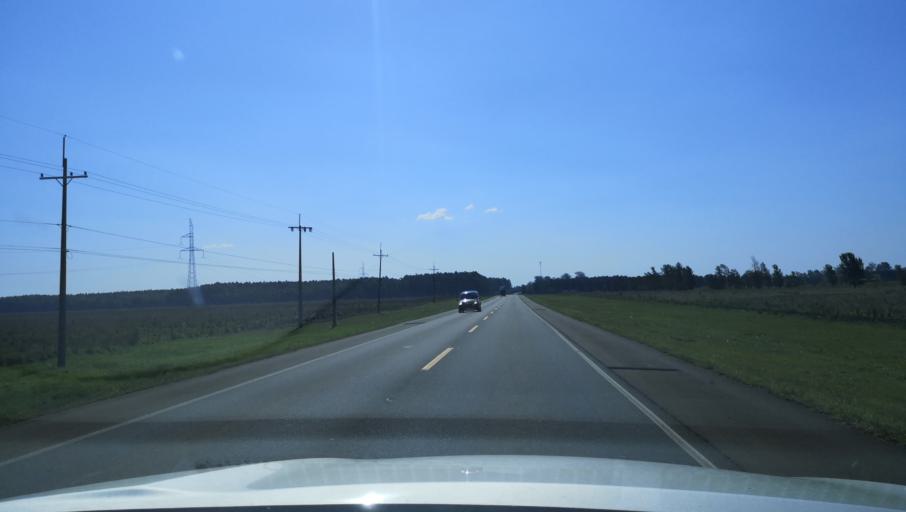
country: PY
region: Itapua
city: General Delgado
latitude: -27.0657
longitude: -56.6176
